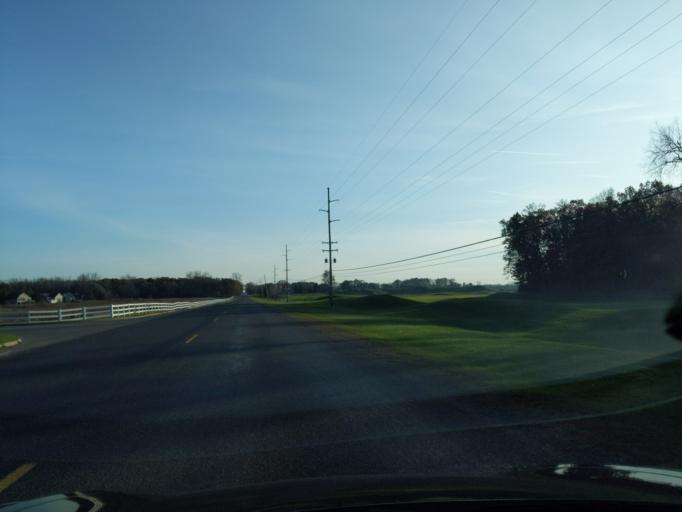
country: US
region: Michigan
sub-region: Clinton County
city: Bath
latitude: 42.7975
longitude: -84.4837
